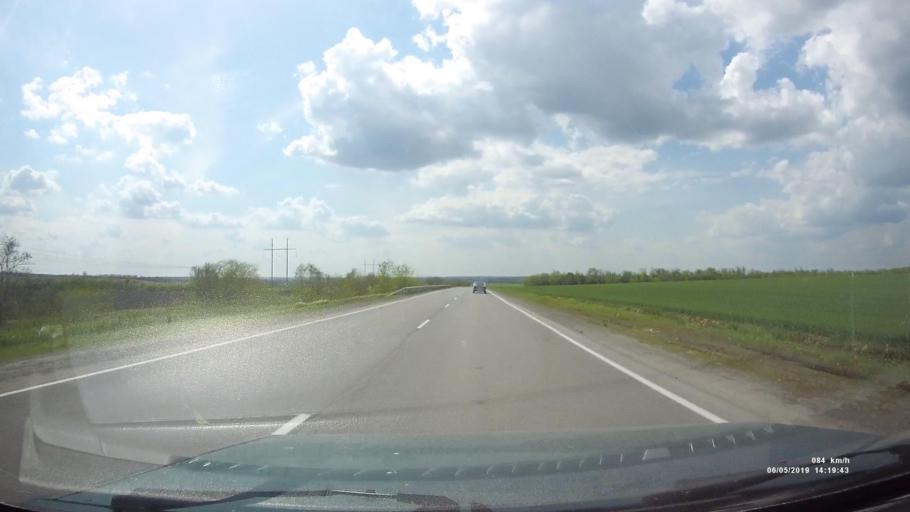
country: RU
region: Rostov
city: Kamenolomni
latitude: 47.6326
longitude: 40.2269
